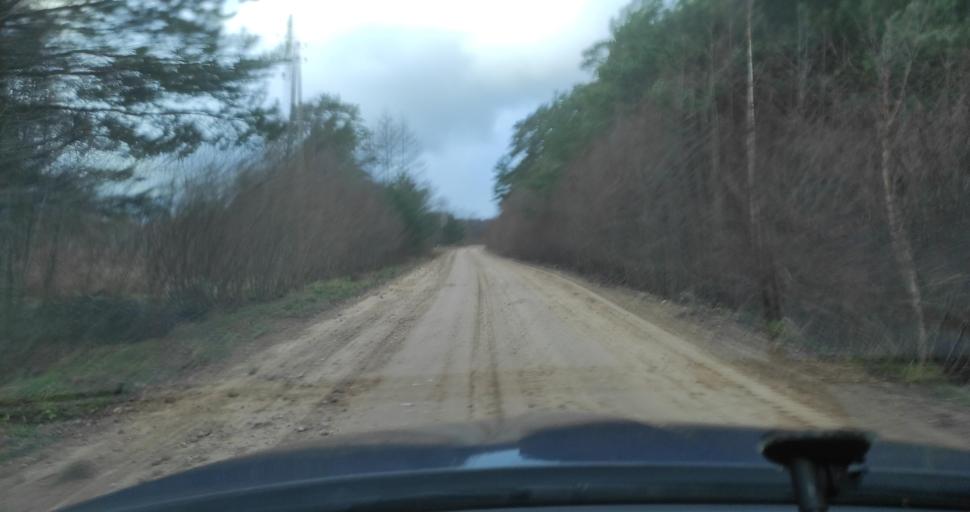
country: LV
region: Pavilostas
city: Pavilosta
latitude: 56.8556
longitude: 21.1345
